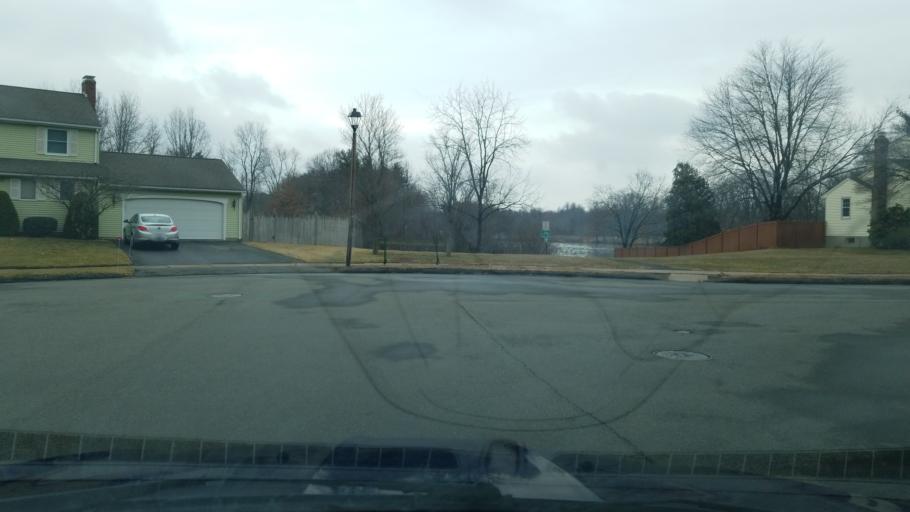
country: US
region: Connecticut
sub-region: Hartford County
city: Wethersfield
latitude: 41.6873
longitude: -72.6675
